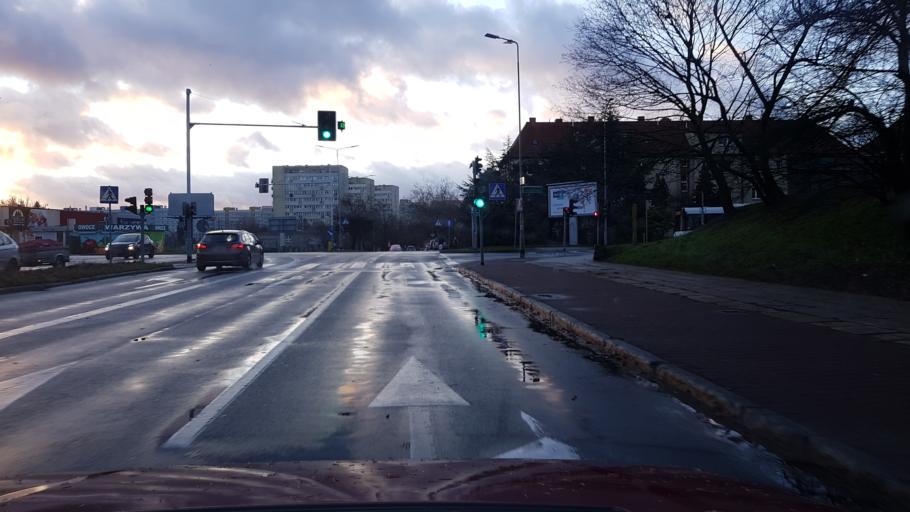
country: PL
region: West Pomeranian Voivodeship
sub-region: Szczecin
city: Szczecin
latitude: 53.4333
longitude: 14.5125
